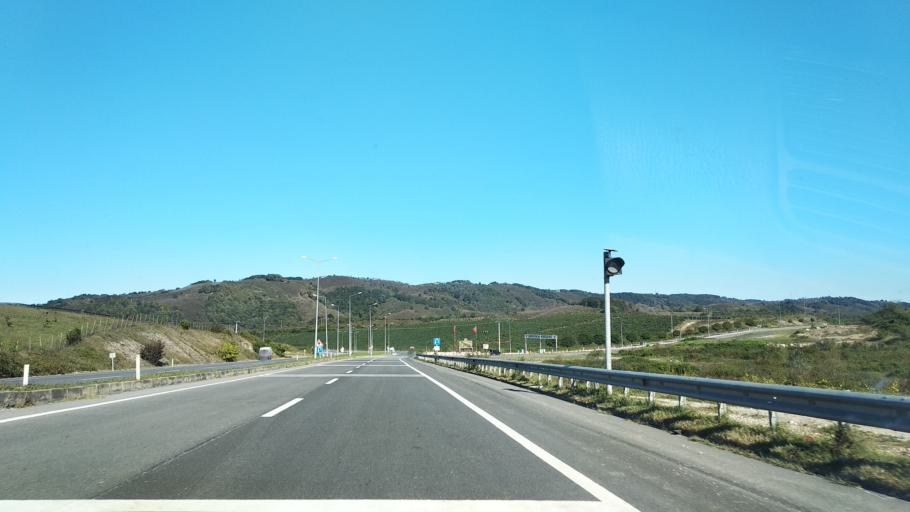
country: TR
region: Sakarya
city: Ortakoy
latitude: 41.0469
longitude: 30.6285
